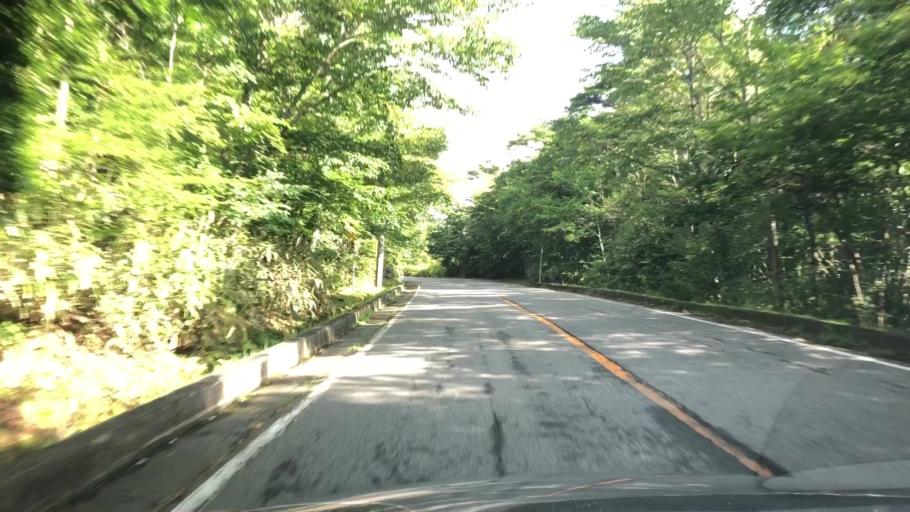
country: JP
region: Shizuoka
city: Gotemba
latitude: 35.3323
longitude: 138.8097
